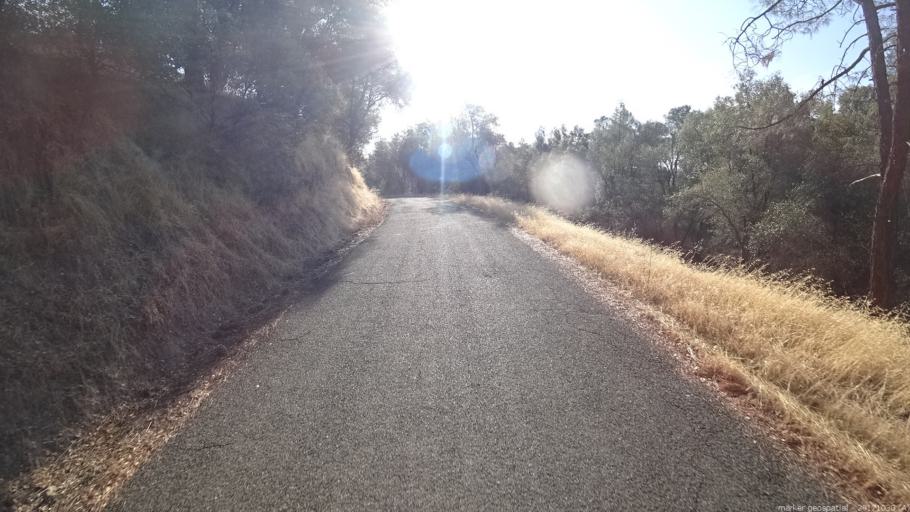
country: US
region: California
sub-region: Shasta County
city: Palo Cedro
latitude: 40.5674
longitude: -122.1384
